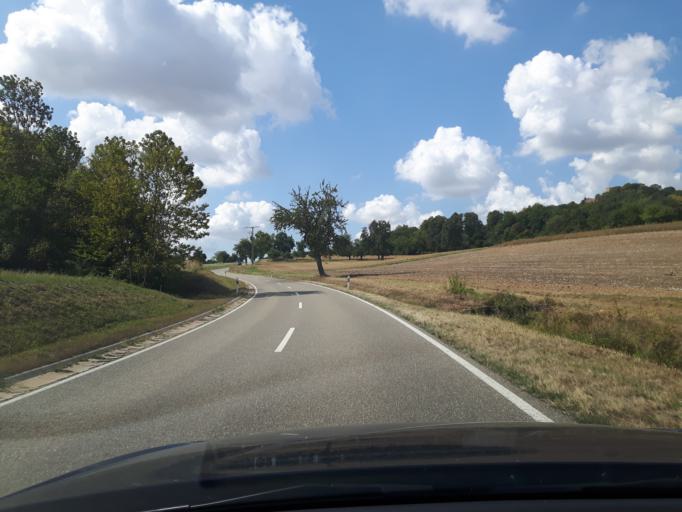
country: DE
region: Baden-Wuerttemberg
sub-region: Karlsruhe Region
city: Sinsheim
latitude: 49.2153
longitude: 8.8888
